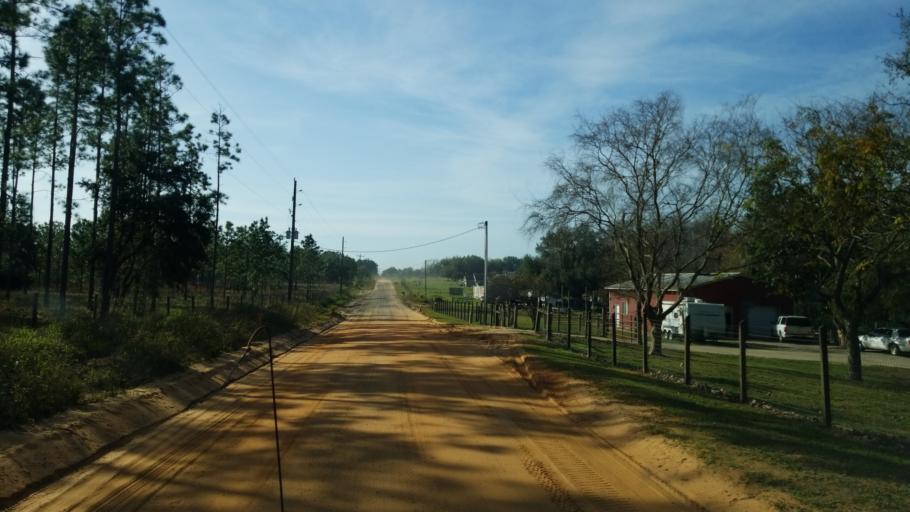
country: US
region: Florida
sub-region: Lake County
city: Clermont
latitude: 28.4567
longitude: -81.7570
